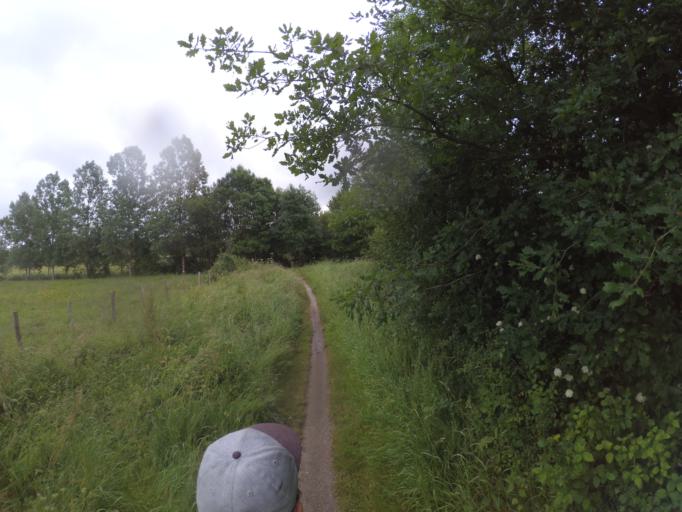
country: FR
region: Pays de la Loire
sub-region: Departement de la Vendee
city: Nesmy
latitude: 46.6160
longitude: -1.4037
